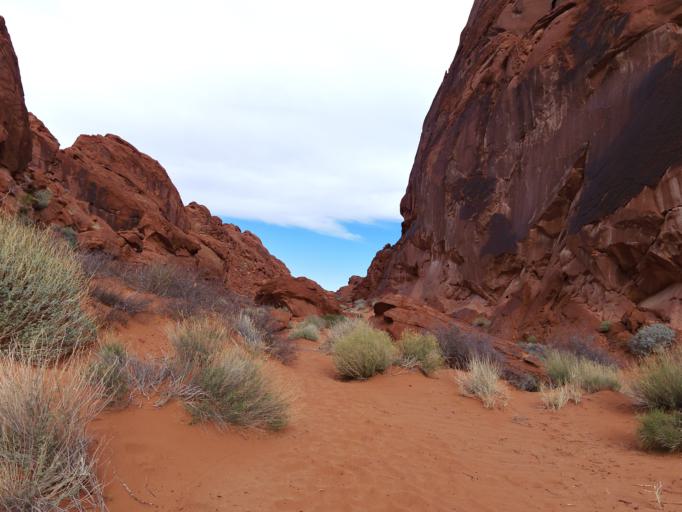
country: US
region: Nevada
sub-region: Clark County
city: Moapa Valley
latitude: 36.4474
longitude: -114.5093
